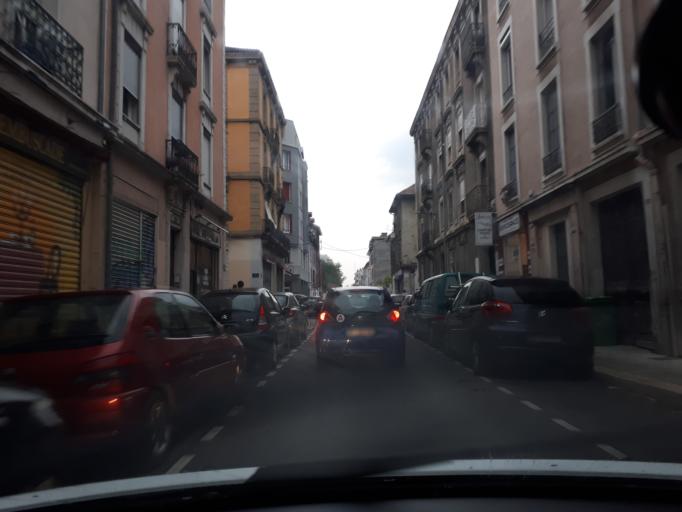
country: FR
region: Rhone-Alpes
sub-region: Departement de l'Isere
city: Saint-Martin-le-Vinoux
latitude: 45.1877
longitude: 5.7111
